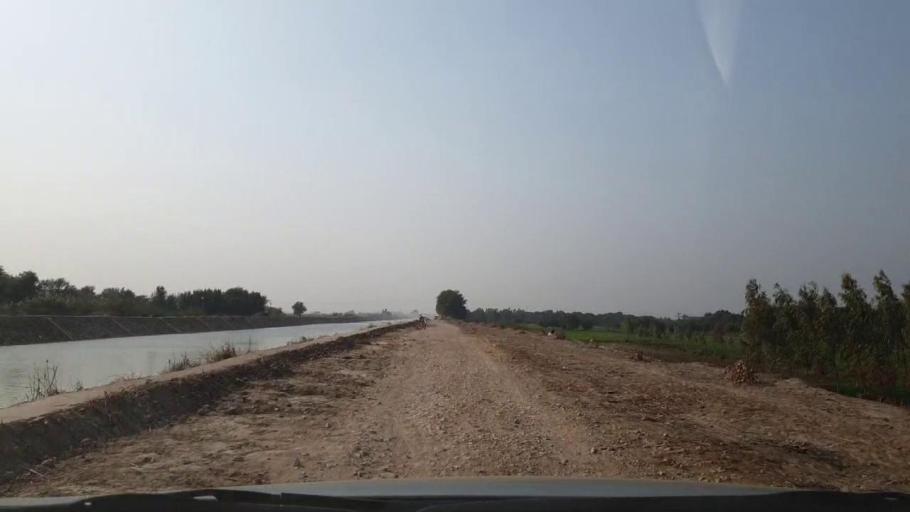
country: PK
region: Sindh
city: Tando Adam
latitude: 25.6390
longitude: 68.5918
